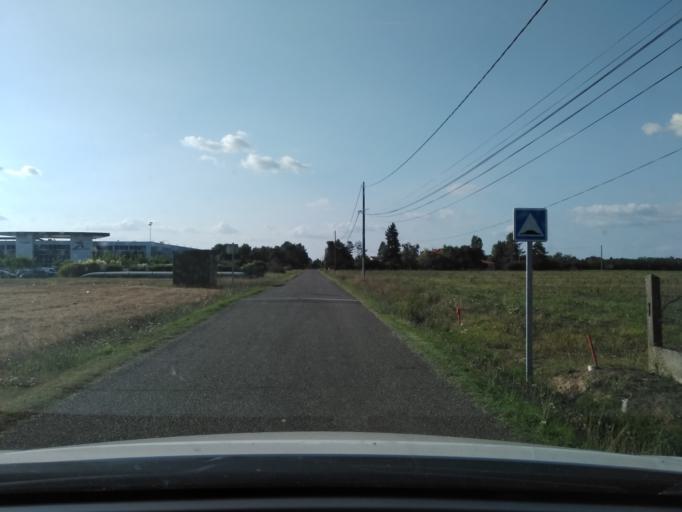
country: FR
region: Midi-Pyrenees
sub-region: Departement du Tarn-et-Garonne
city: Montech
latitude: 43.9644
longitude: 1.2477
